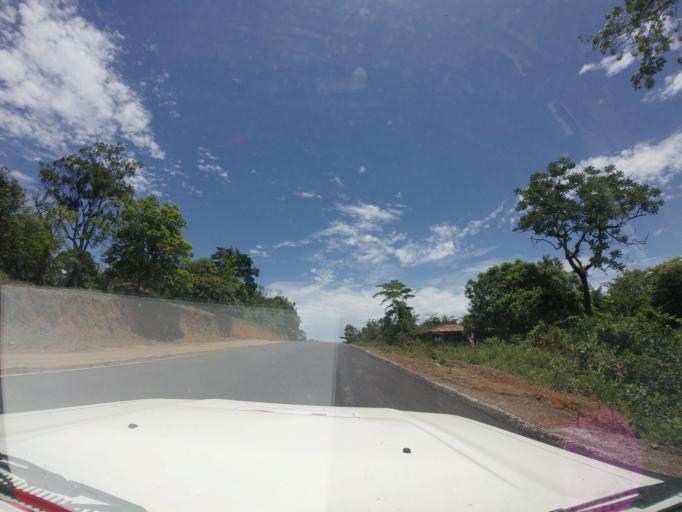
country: LR
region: Margibi
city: Kakata
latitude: 6.7791
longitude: -9.9724
